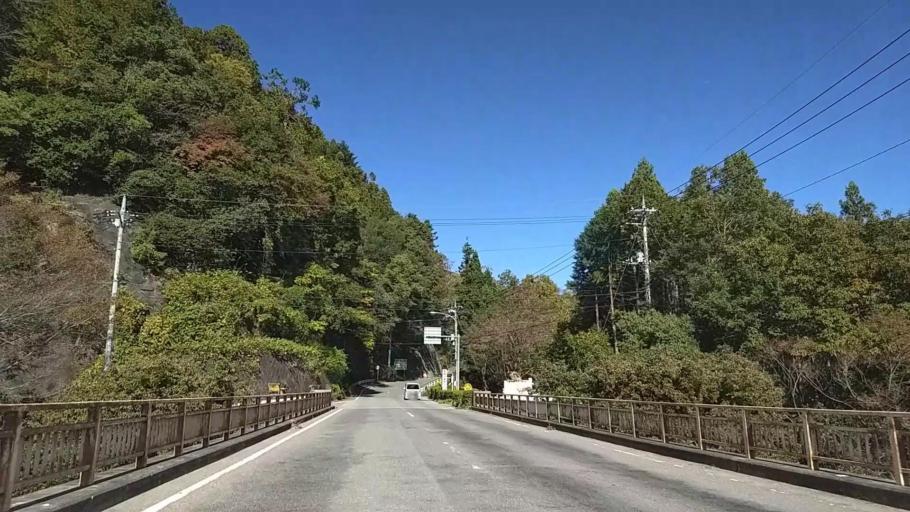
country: JP
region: Yamanashi
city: Uenohara
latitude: 35.6473
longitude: 139.0969
